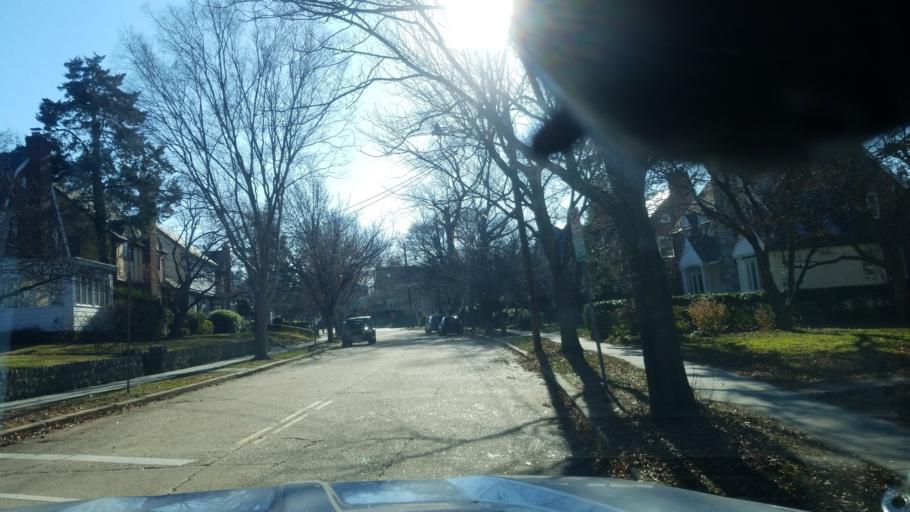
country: US
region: Maryland
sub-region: Montgomery County
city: Silver Spring
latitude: 38.9822
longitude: -77.0315
